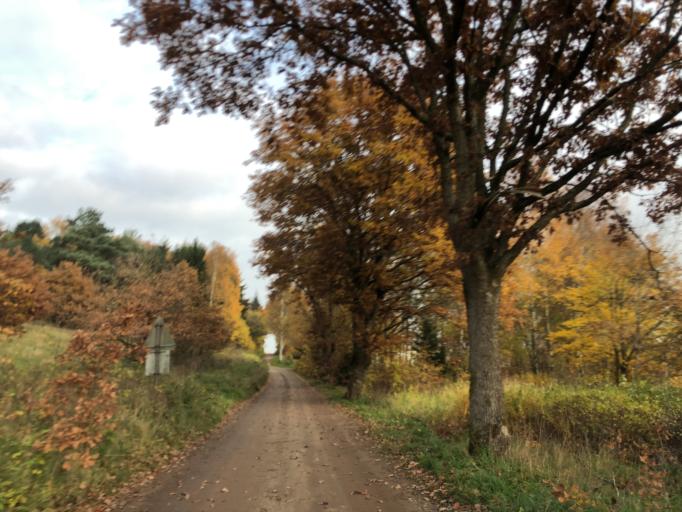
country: DK
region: Central Jutland
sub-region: Silkeborg Kommune
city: Silkeborg
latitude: 56.1455
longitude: 9.4864
